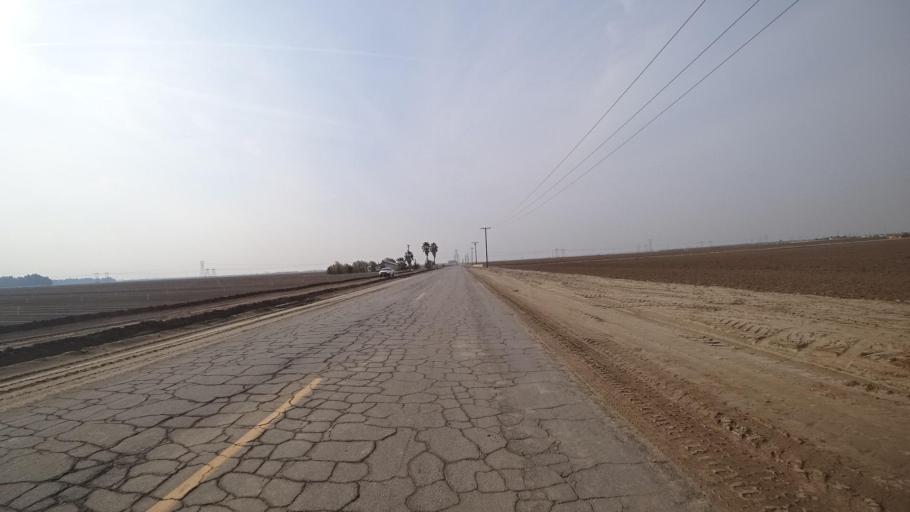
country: US
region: California
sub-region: Kern County
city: Weedpatch
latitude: 35.1511
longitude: -118.8990
